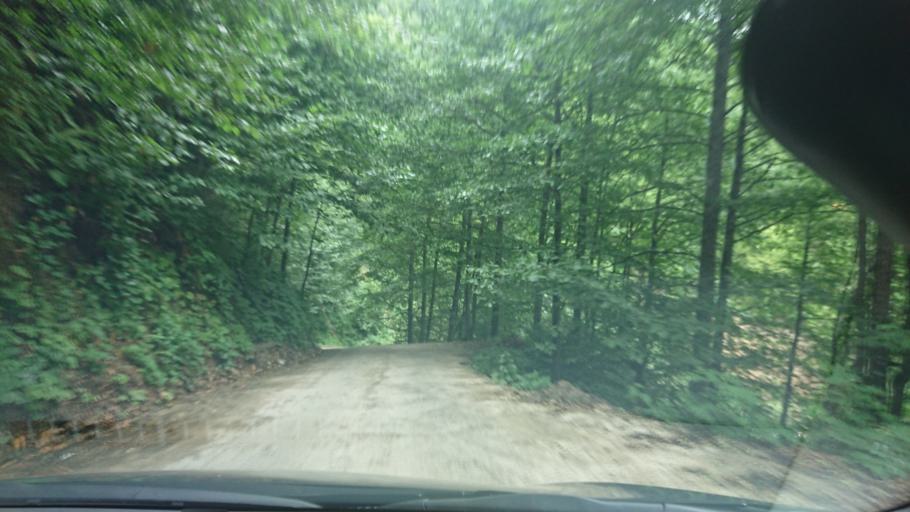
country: TR
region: Gumushane
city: Kurtun
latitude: 40.6750
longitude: 39.0430
